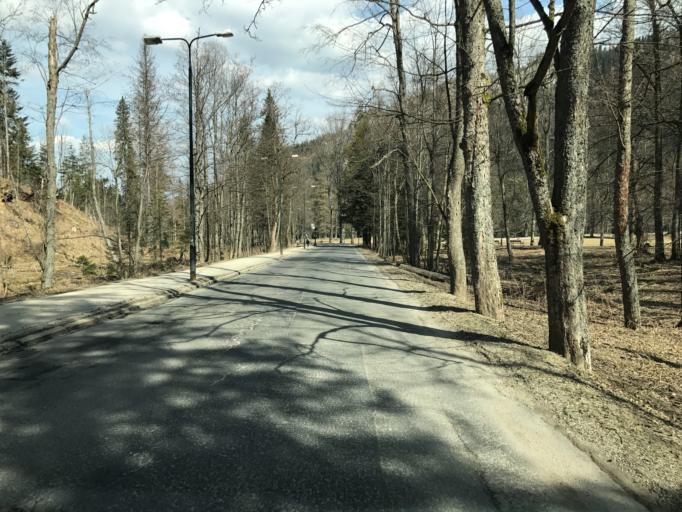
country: PL
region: Lesser Poland Voivodeship
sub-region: Powiat tatrzanski
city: Zakopane
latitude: 49.2717
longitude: 19.9805
